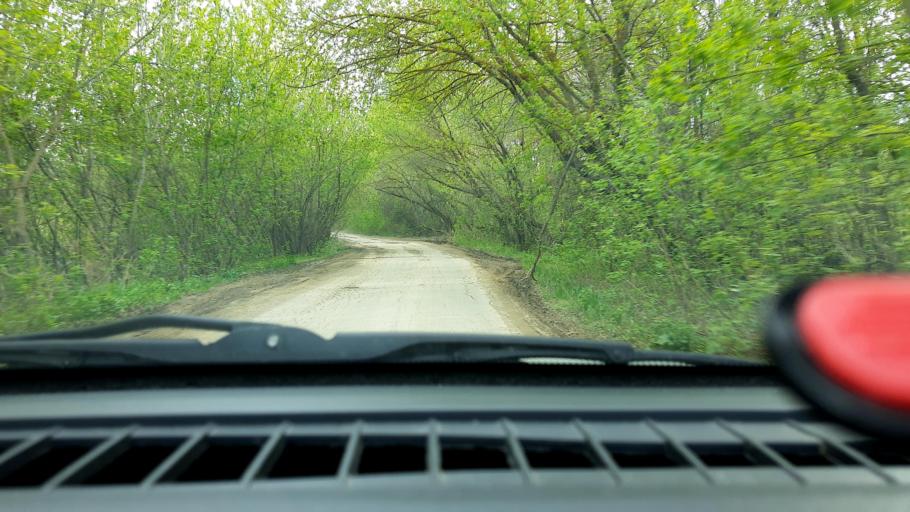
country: RU
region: Nizjnij Novgorod
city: Neklyudovo
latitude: 56.3901
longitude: 43.8427
